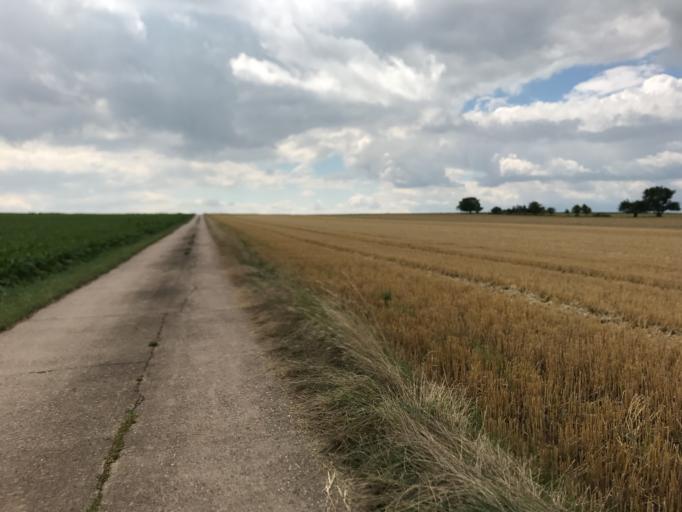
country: DE
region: Rheinland-Pfalz
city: Essenheim
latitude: 49.9444
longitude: 8.1505
